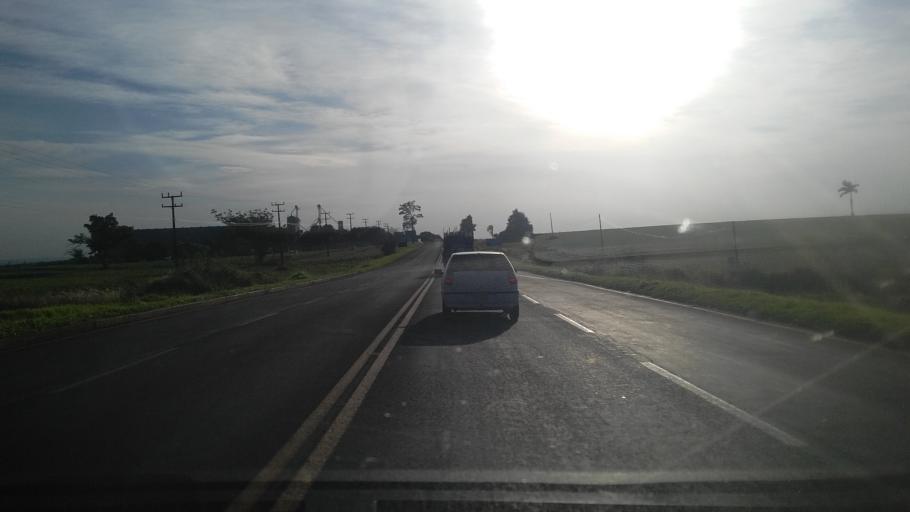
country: BR
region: Parana
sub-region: Bandeirantes
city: Bandeirantes
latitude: -23.1450
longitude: -50.5800
